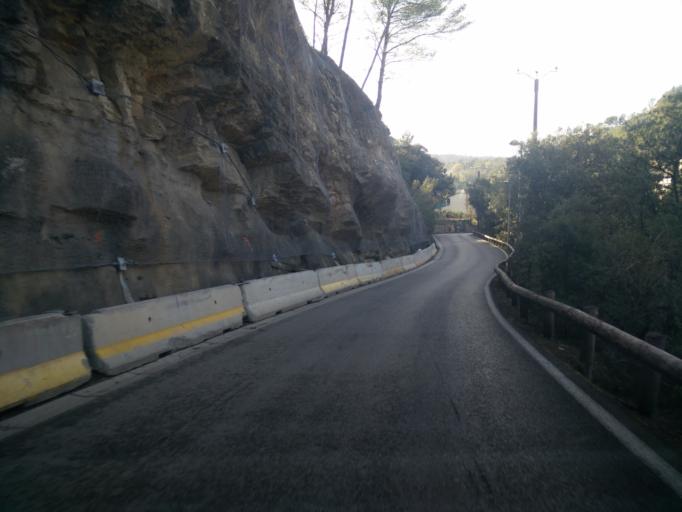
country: FR
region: Provence-Alpes-Cote d'Azur
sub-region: Departement du Var
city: Sollies-Toucas
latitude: 43.2023
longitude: 6.0213
